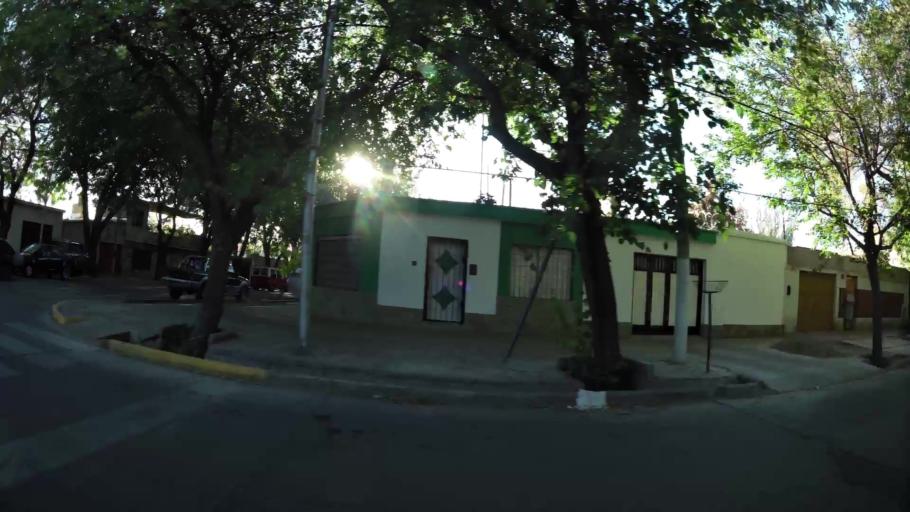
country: AR
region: Mendoza
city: Las Heras
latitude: -32.8644
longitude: -68.8381
